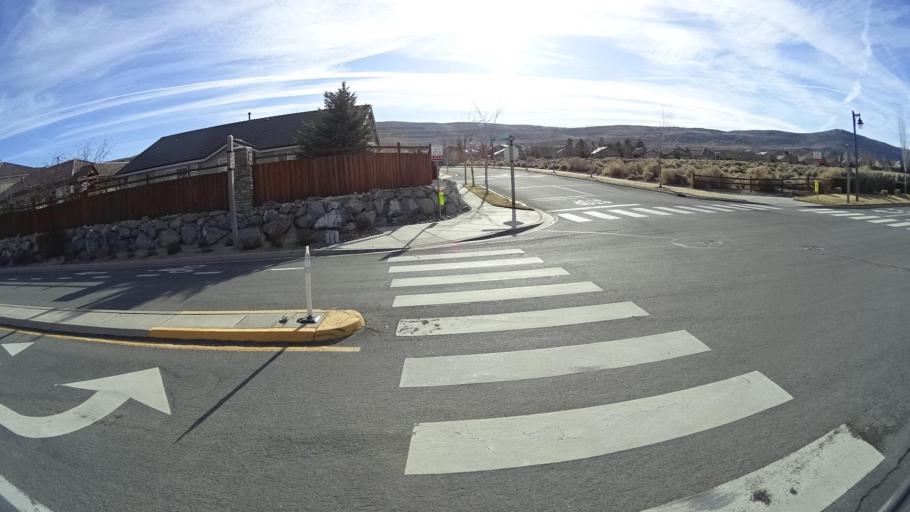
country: US
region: Nevada
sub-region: Washoe County
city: Spanish Springs
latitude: 39.6190
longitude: -119.6703
